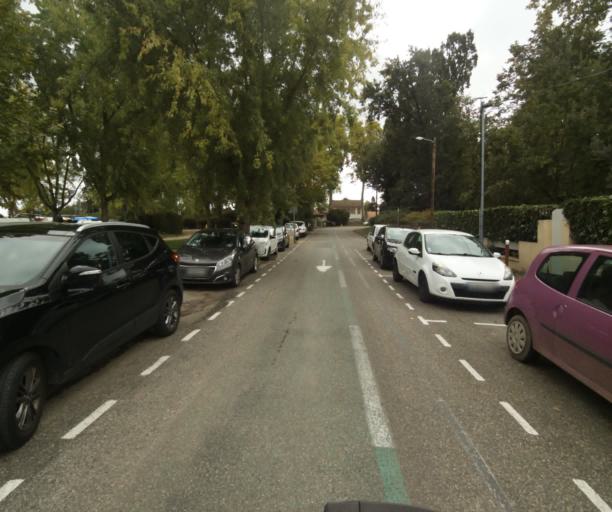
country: FR
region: Midi-Pyrenees
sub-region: Departement du Tarn-et-Garonne
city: Montech
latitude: 43.9603
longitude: 1.2362
